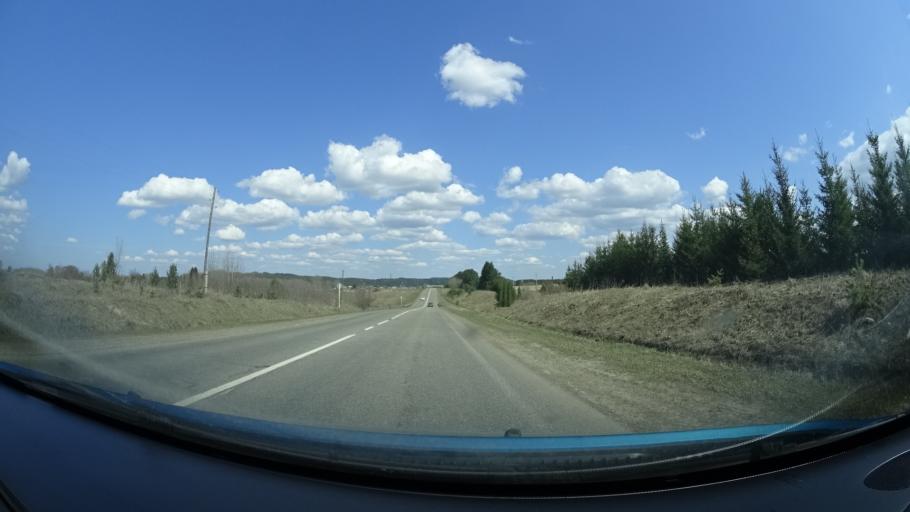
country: RU
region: Perm
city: Osa
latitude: 57.2844
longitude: 55.5677
